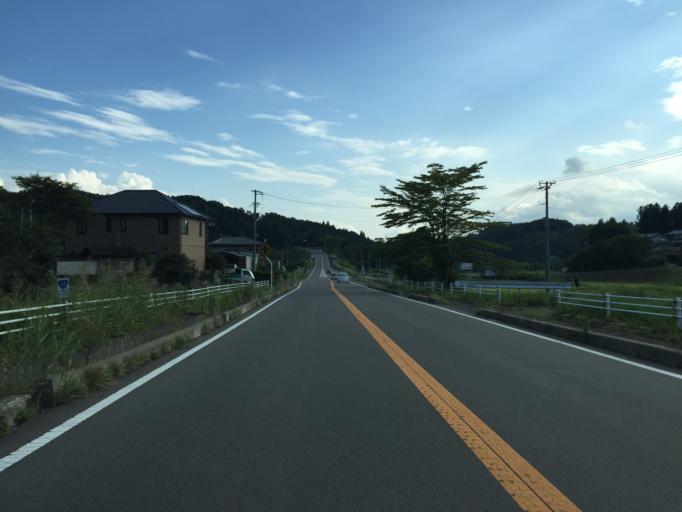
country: JP
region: Fukushima
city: Fukushima-shi
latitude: 37.6931
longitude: 140.5248
